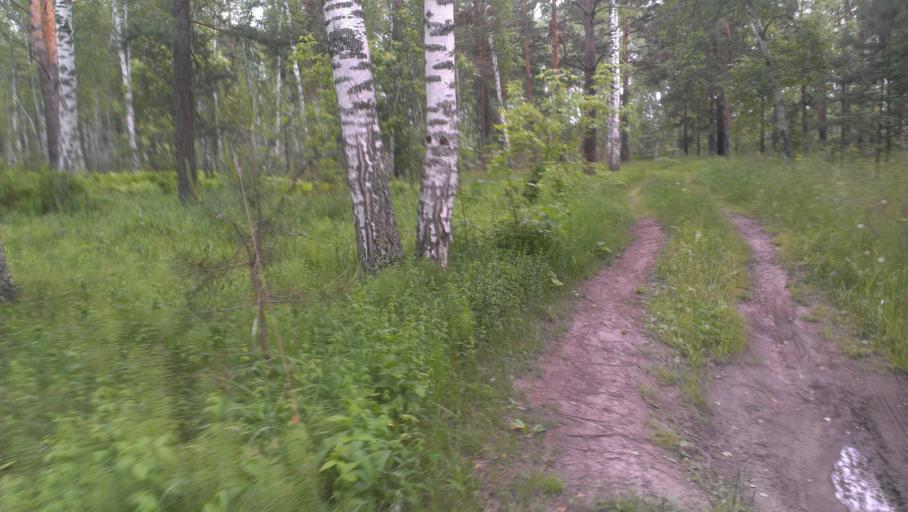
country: RU
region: Altai Krai
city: Sannikovo
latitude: 53.3385
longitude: 84.0503
